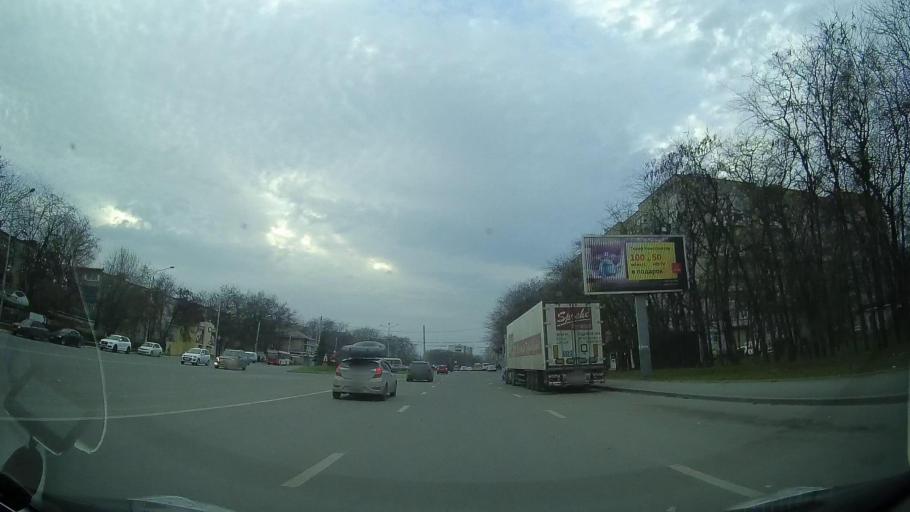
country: RU
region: Rostov
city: Aksay
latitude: 47.2400
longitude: 39.8324
